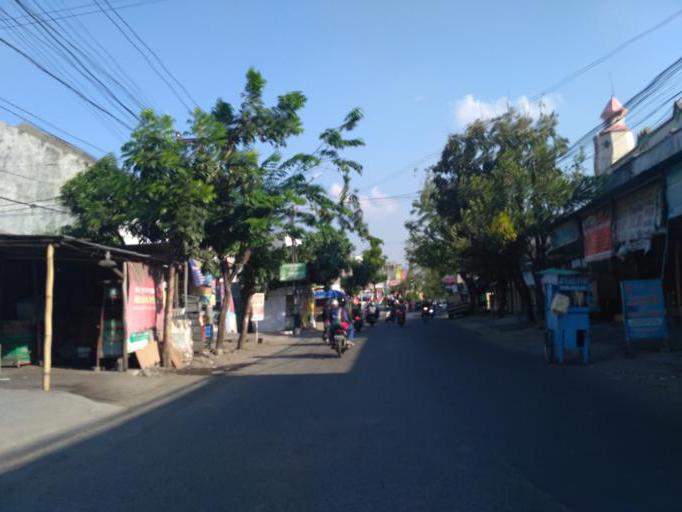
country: ID
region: Central Java
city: Semarang
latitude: -6.9876
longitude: 110.4482
